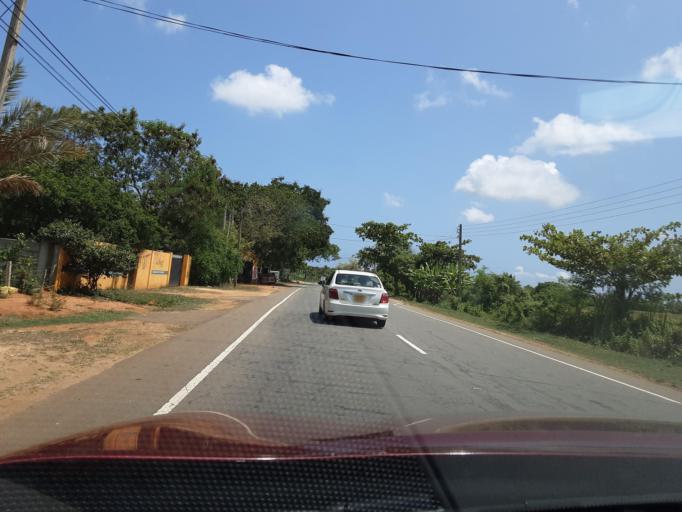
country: LK
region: Southern
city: Tangalla
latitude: 6.2390
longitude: 81.2270
